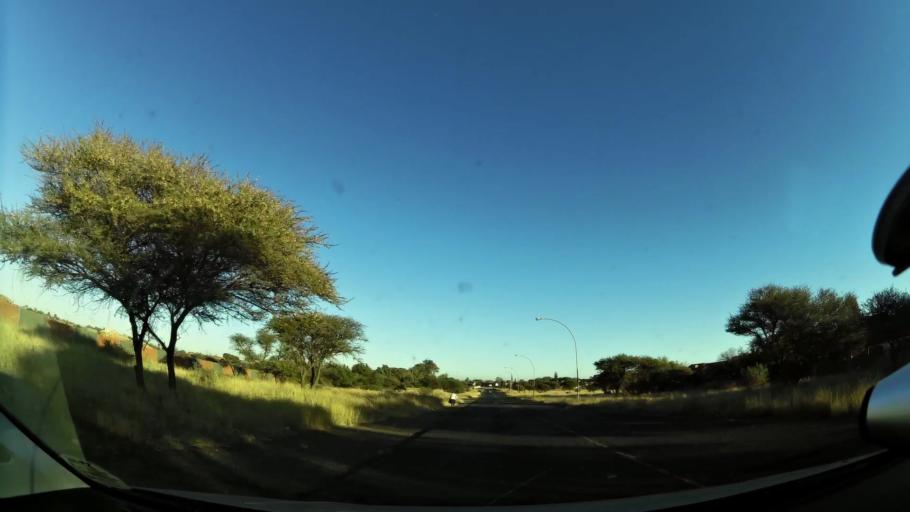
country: ZA
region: Northern Cape
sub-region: Frances Baard District Municipality
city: Kimberley
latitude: -28.7629
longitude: 24.7497
